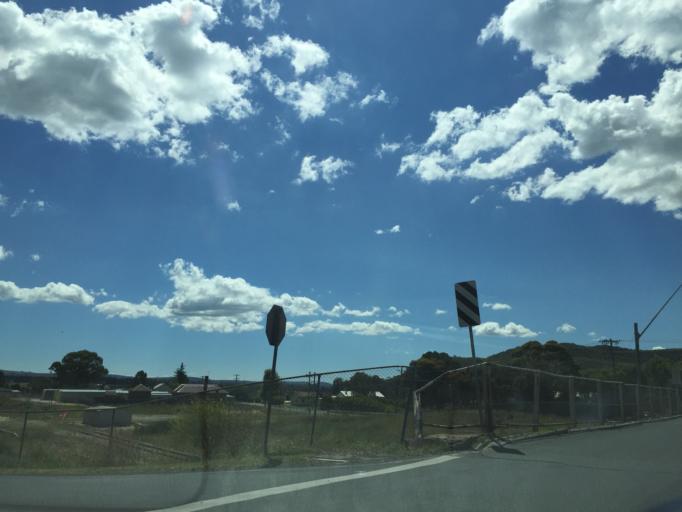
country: AU
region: New South Wales
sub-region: Lithgow
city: Portland
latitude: -33.4114
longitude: 150.0644
